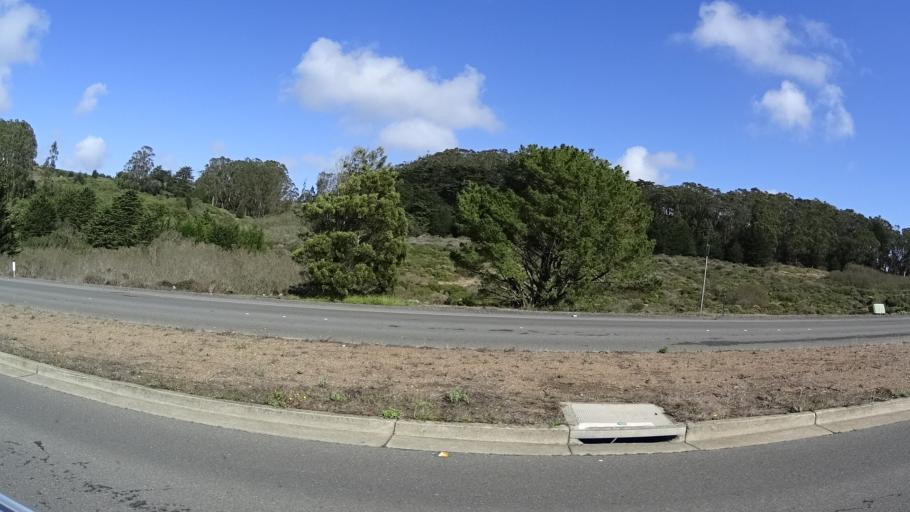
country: US
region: California
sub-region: San Mateo County
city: Daly City
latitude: 37.6973
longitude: -122.4380
